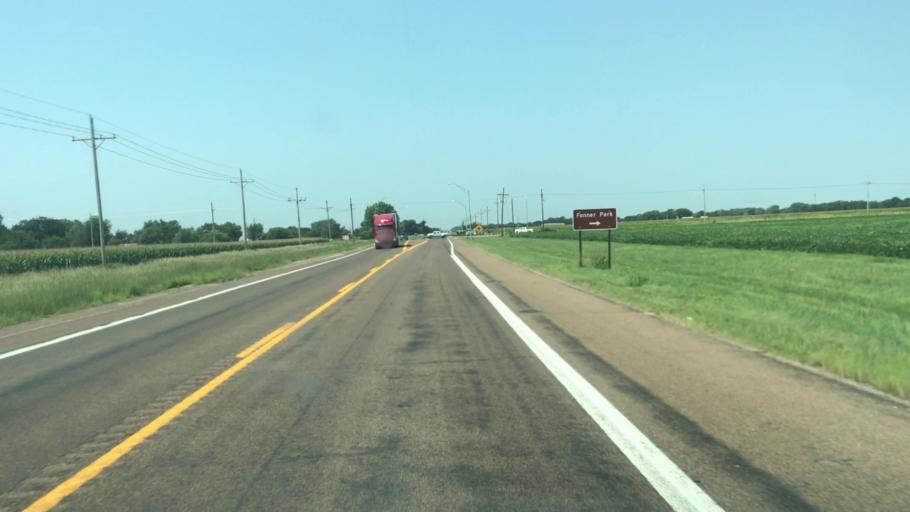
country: US
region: Nebraska
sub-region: Hall County
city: Grand Island
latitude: 40.8869
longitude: -98.3178
